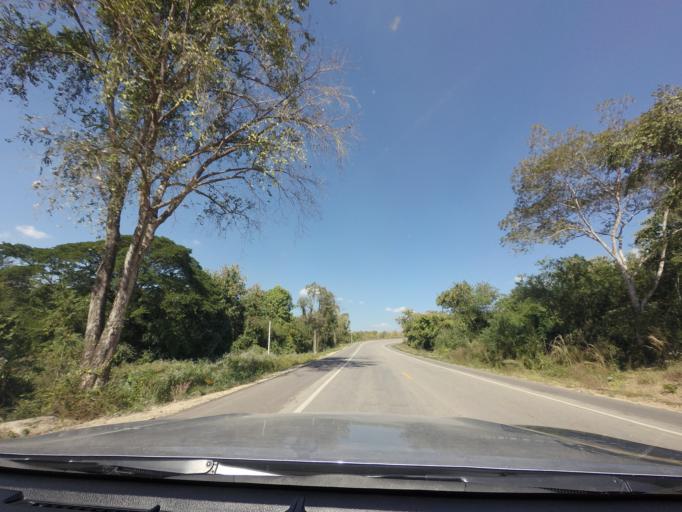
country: TH
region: Lampang
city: Mae Mo
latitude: 18.4821
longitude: 99.6355
